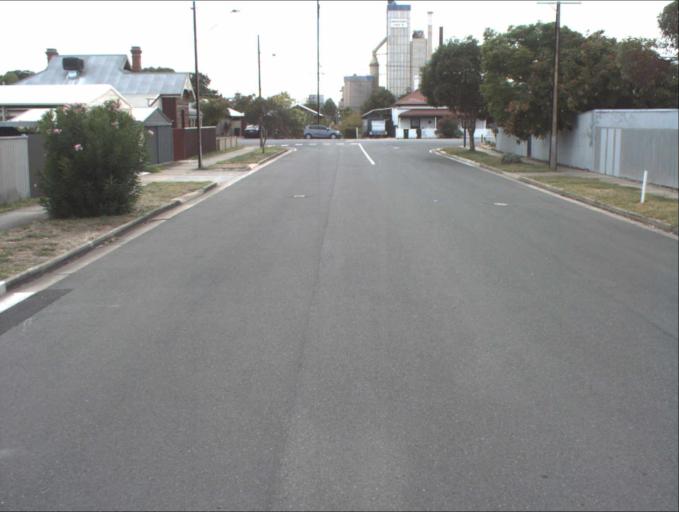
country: AU
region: South Australia
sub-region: Port Adelaide Enfield
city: Birkenhead
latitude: -34.8317
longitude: 138.4957
